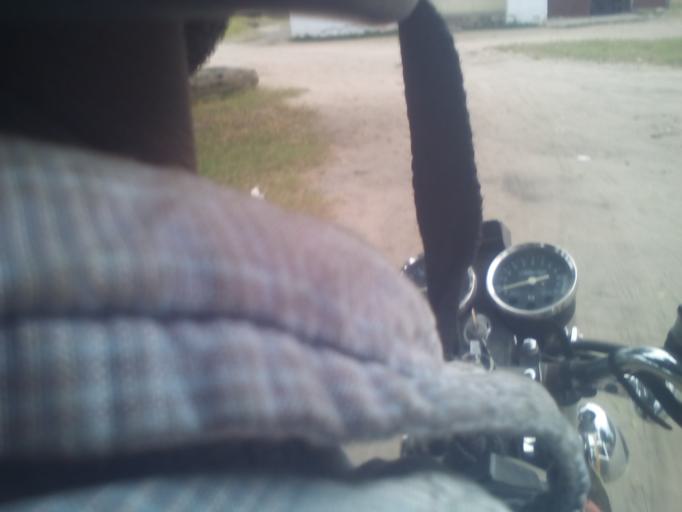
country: TZ
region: Dar es Salaam
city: Dar es Salaam
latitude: -6.8482
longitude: 39.2772
